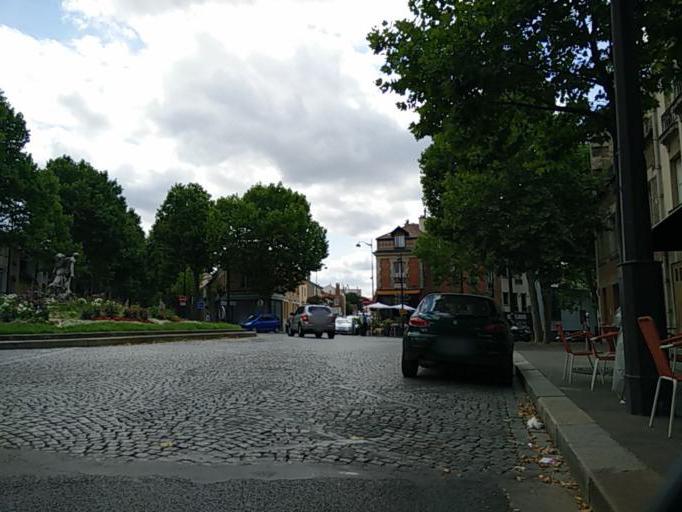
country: FR
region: Ile-de-France
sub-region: Departement de Seine-Saint-Denis
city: Le Pre-Saint-Gervais
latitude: 48.8822
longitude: 2.3935
